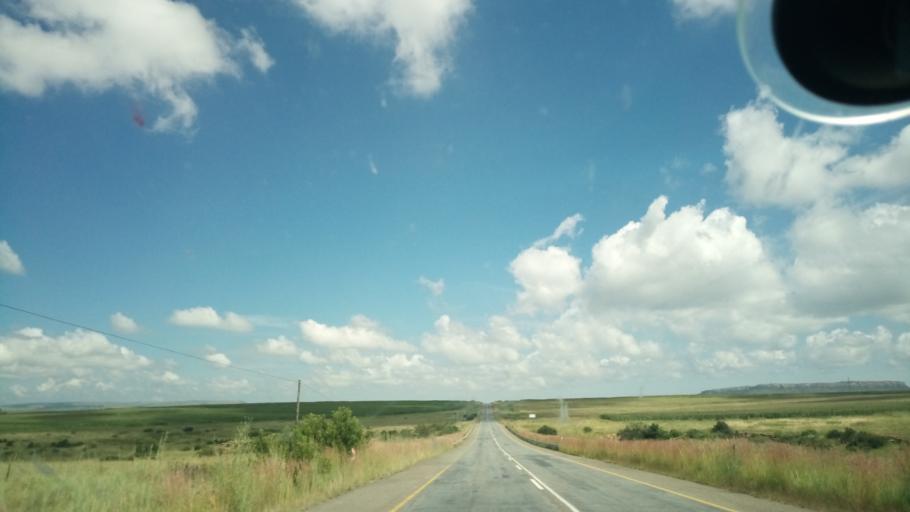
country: ZA
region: Orange Free State
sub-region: Thabo Mofutsanyana District Municipality
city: Ficksburg
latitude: -28.9019
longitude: 27.7928
